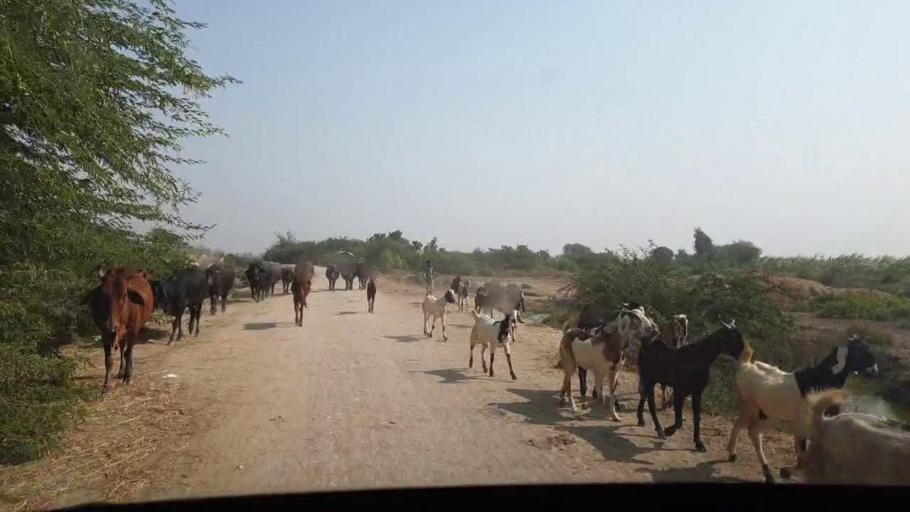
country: PK
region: Sindh
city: Chuhar Jamali
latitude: 24.2656
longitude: 67.9438
